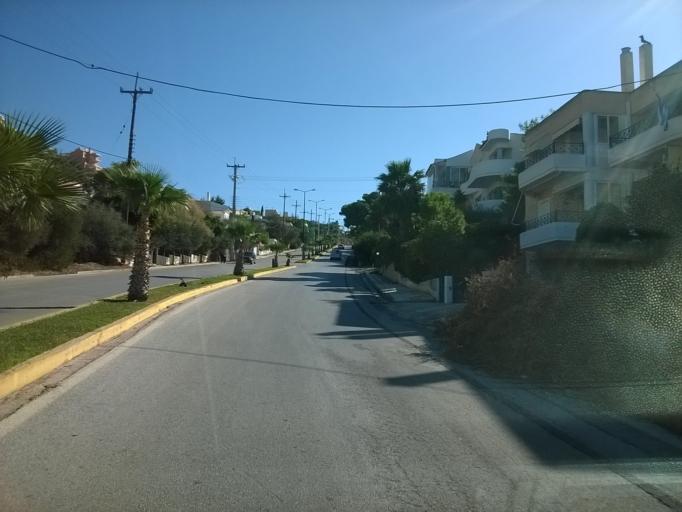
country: GR
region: Attica
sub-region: Nomarchia Anatolikis Attikis
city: Saronida
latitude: 37.7459
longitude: 23.9191
